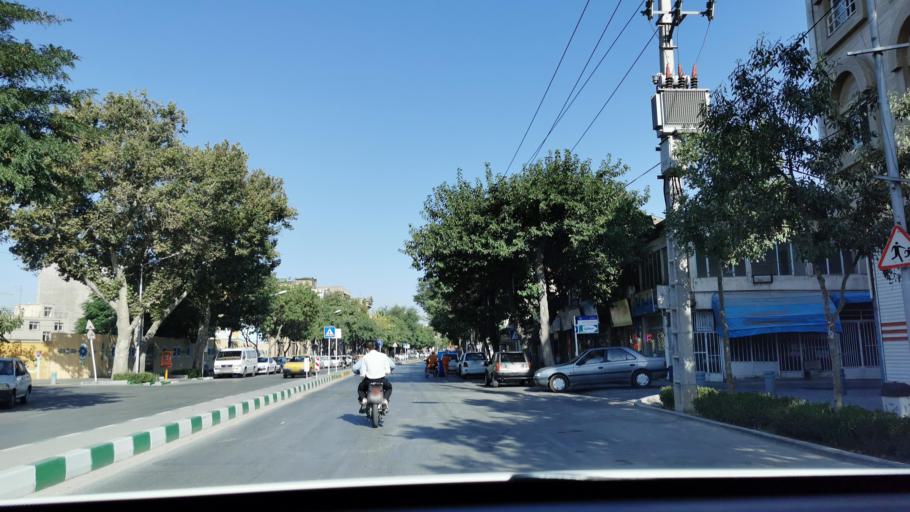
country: IR
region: Razavi Khorasan
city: Mashhad
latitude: 36.2968
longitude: 59.6244
